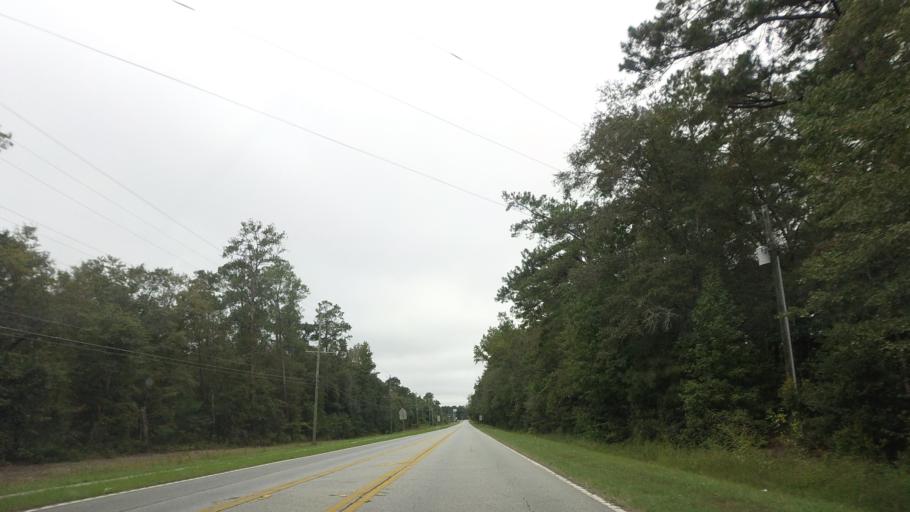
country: US
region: Georgia
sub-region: Lowndes County
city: Valdosta
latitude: 30.8632
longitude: -83.2515
